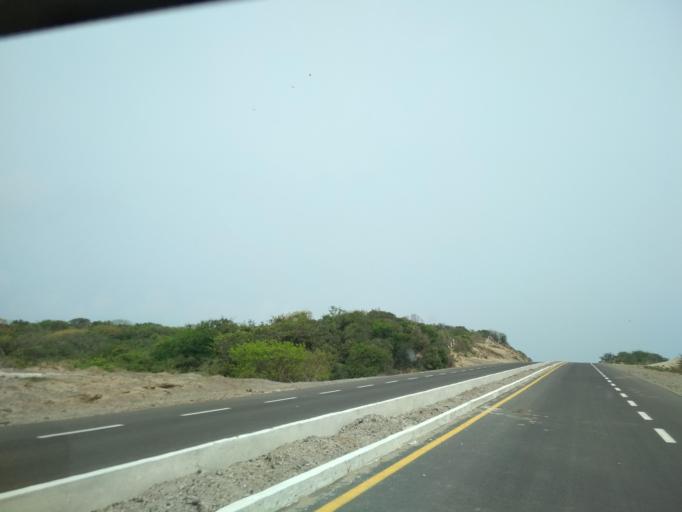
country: MX
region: Veracruz
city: Anton Lizardo
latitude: 19.0480
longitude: -96.0008
